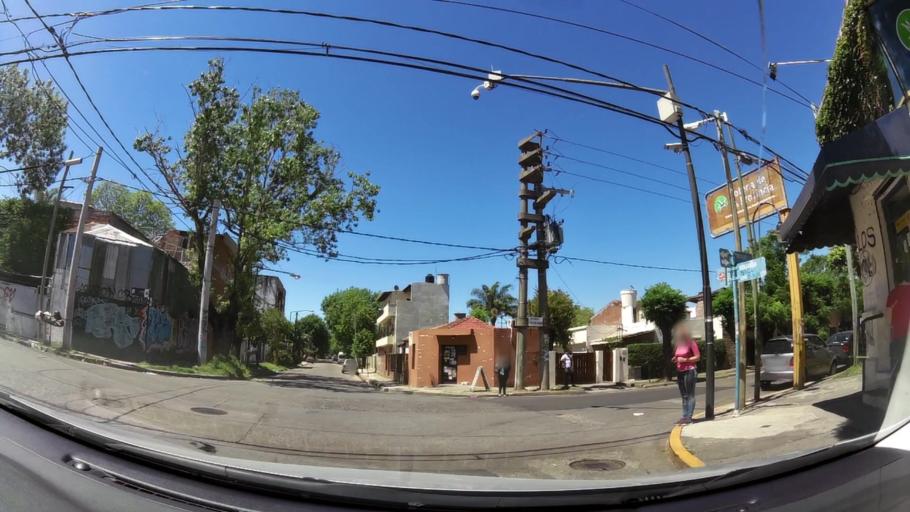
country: AR
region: Buenos Aires
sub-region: Partido de San Isidro
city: San Isidro
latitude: -34.4582
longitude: -58.5391
